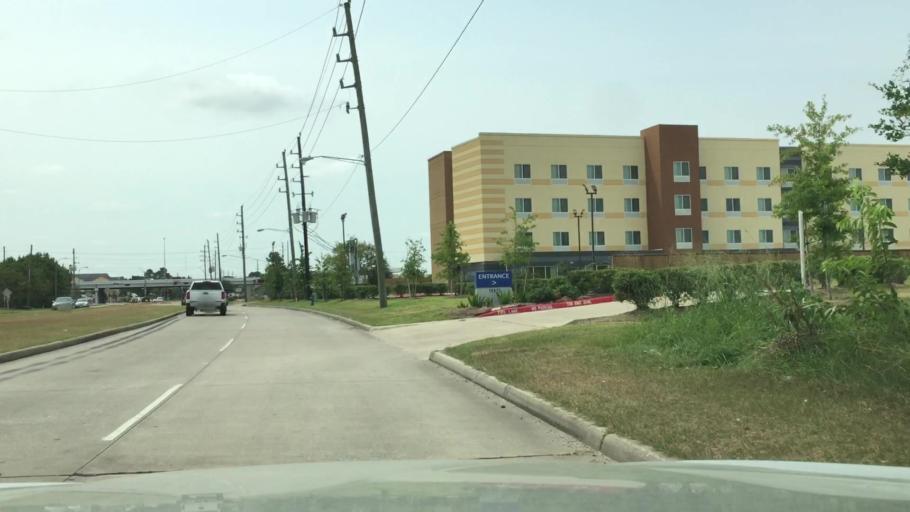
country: US
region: Texas
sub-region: Harris County
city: Jersey Village
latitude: 29.9328
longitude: -95.5458
